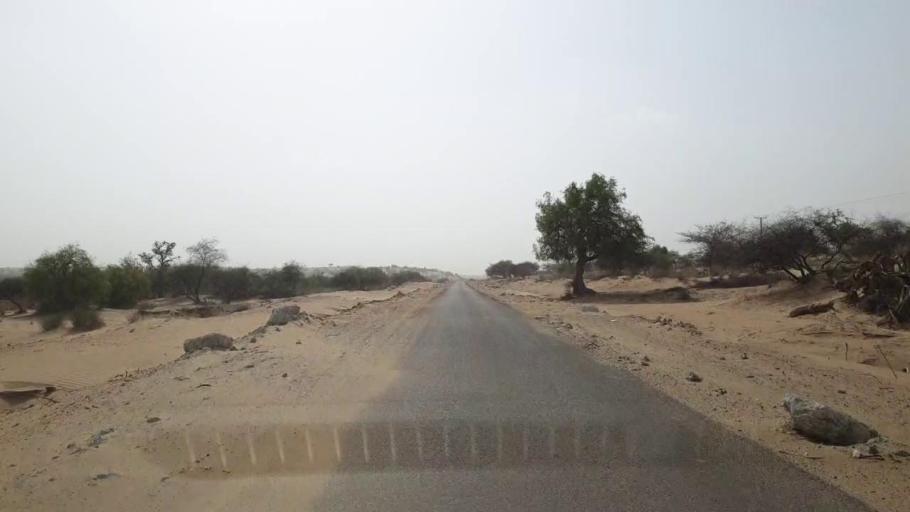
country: PK
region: Sindh
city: Mithi
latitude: 24.6218
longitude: 69.8755
